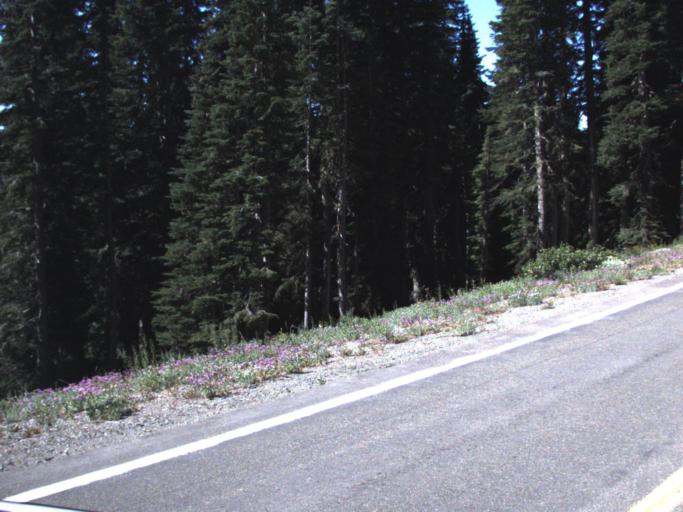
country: US
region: Washington
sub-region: King County
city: Enumclaw
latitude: 46.8711
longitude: -121.5300
